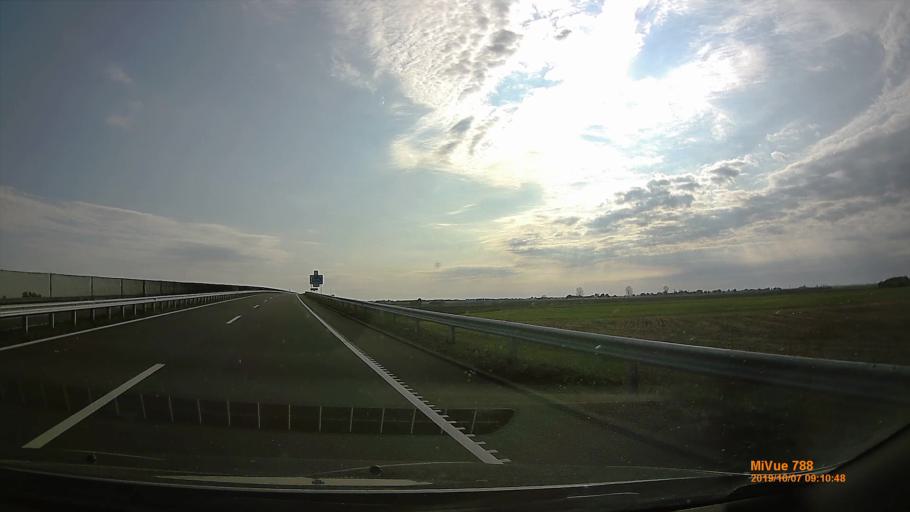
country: HU
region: Bekes
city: Szarvas
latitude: 46.8129
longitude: 20.6652
